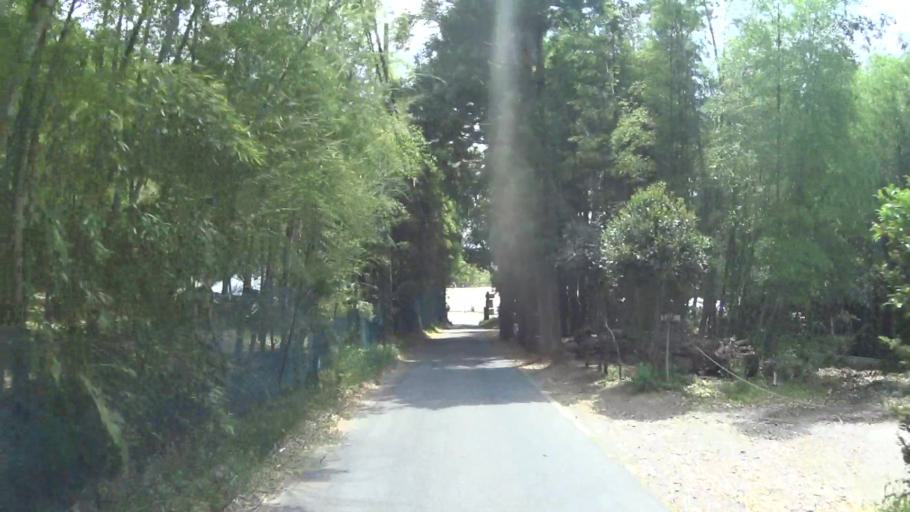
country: JP
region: Kyoto
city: Muko
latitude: 34.9621
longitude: 135.6524
